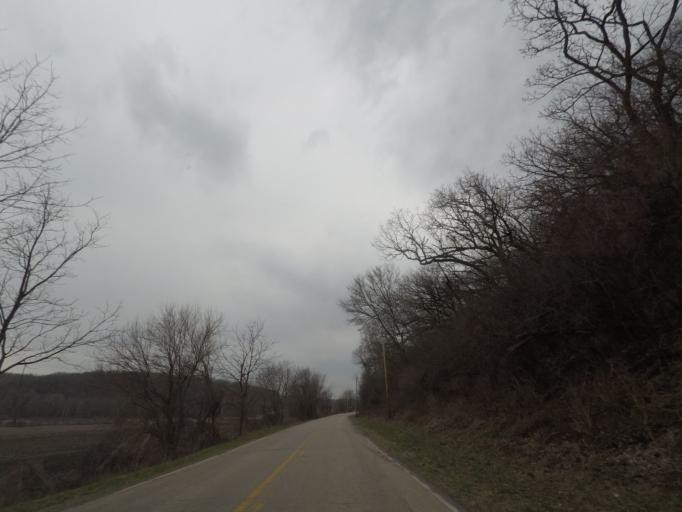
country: US
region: Wisconsin
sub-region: Dane County
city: Cross Plains
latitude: 43.0975
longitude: -89.6023
